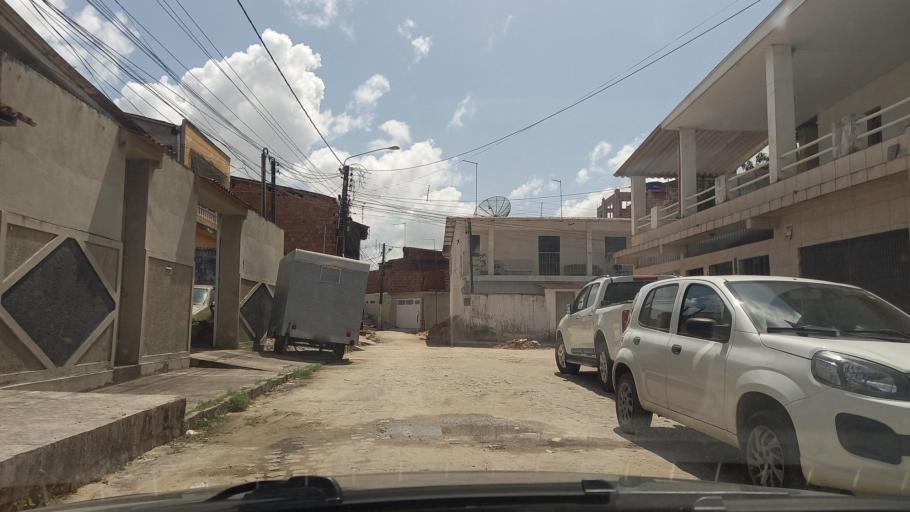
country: BR
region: Pernambuco
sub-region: Goiana
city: Goiana
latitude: -7.5619
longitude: -34.9930
